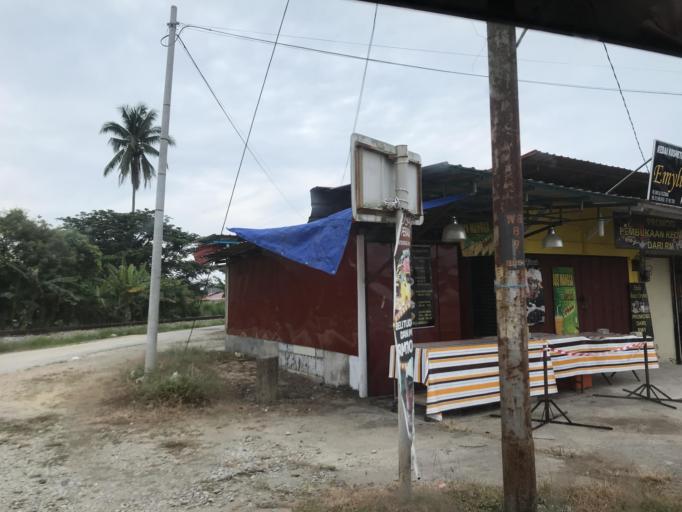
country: MY
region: Kelantan
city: Kota Bharu
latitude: 6.1198
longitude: 102.2021
